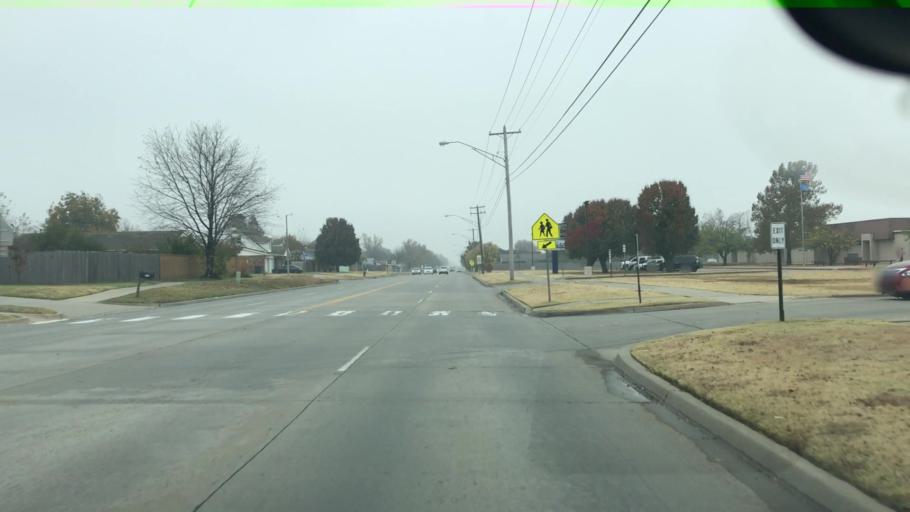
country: US
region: Oklahoma
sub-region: Cleveland County
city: Moore
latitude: 35.3463
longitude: -97.5122
